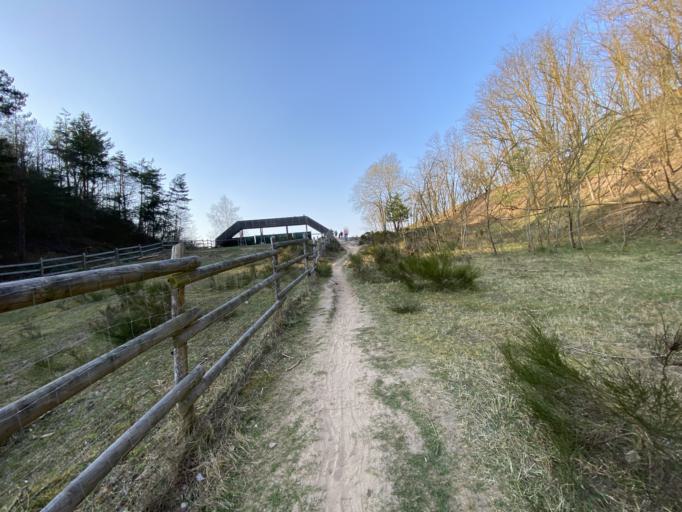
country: DE
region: Bavaria
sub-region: Regierungsbezirk Mittelfranken
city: Buckenhof
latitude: 49.5572
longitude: 11.0596
